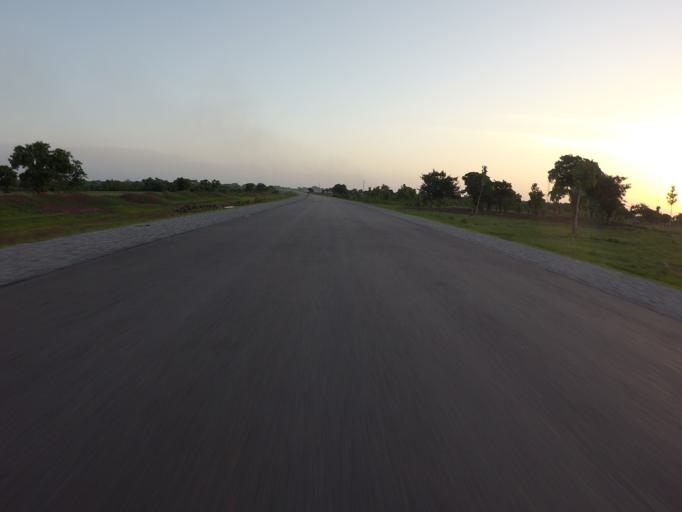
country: GH
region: Northern
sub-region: Yendi
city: Yendi
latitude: 9.9606
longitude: -0.1457
